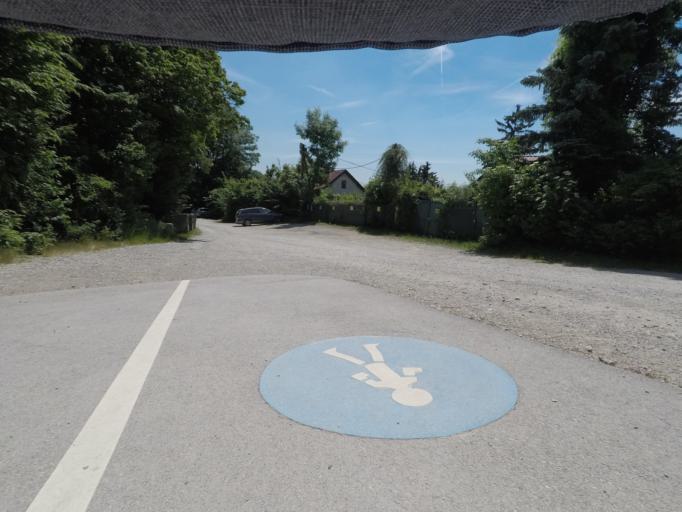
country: AT
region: Lower Austria
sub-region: Politischer Bezirk Modling
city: Perchtoldsdorf
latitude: 48.1769
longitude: 16.2528
